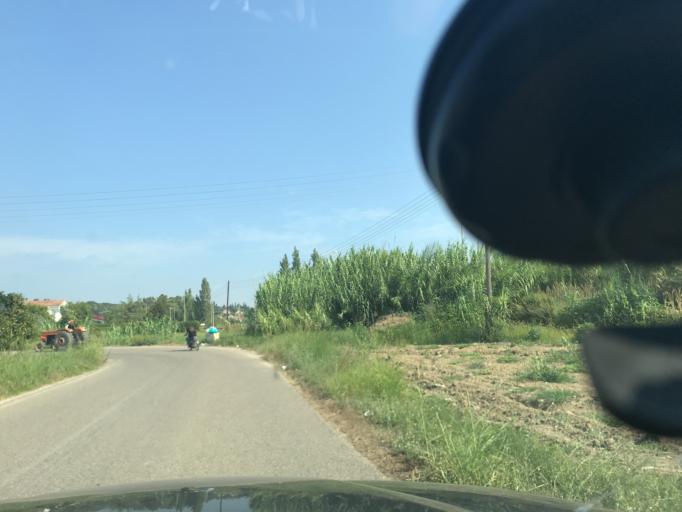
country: GR
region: West Greece
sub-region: Nomos Ileias
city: Kardamas
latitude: 37.7192
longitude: 21.3690
